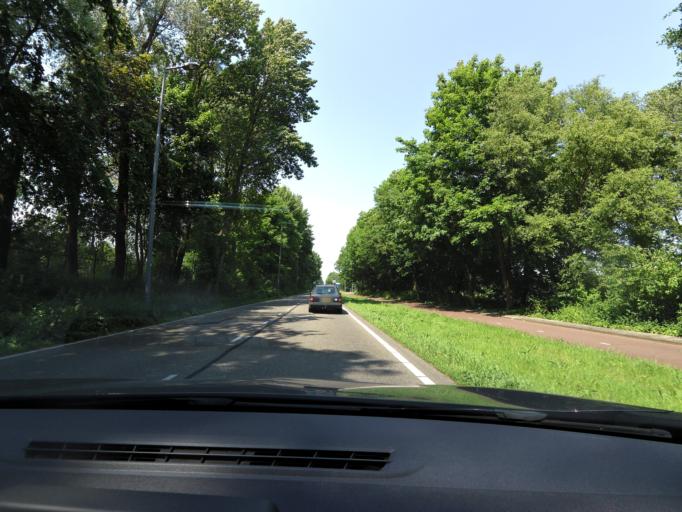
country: NL
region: South Holland
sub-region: Gemeente Rotterdam
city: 's-Gravenland
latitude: 51.9307
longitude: 4.5334
